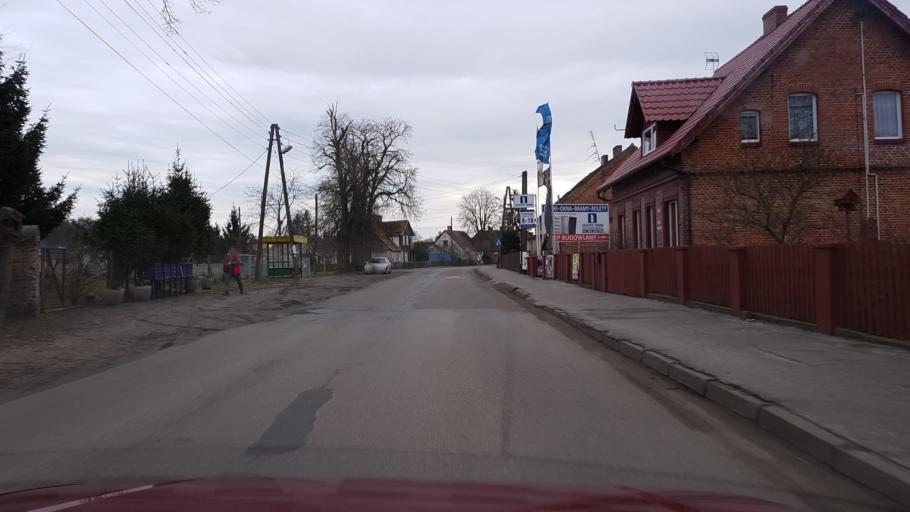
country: PL
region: West Pomeranian Voivodeship
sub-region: Powiat policki
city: Dobra
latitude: 53.5427
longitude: 14.4661
